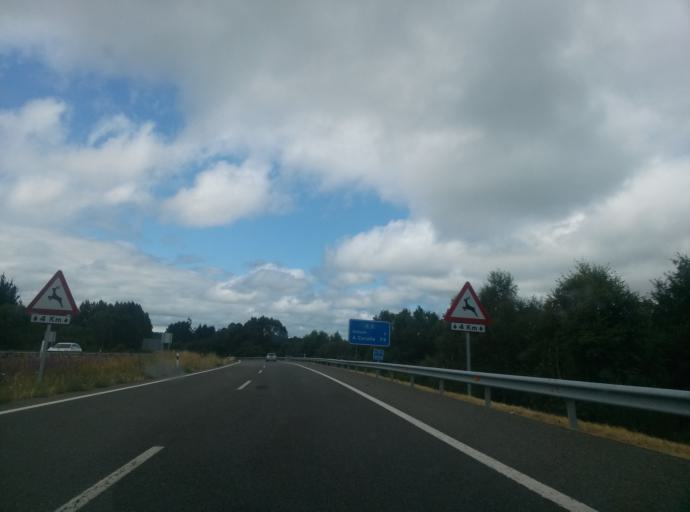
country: ES
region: Galicia
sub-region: Provincia de Lugo
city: Rabade
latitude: 43.1127
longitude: -7.6049
